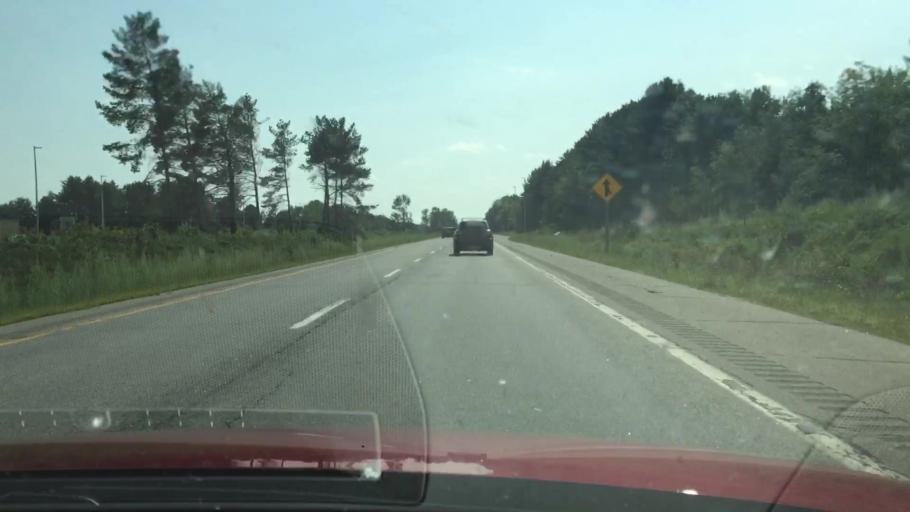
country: US
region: Maine
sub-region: Somerset County
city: Fairfield
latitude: 44.5931
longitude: -69.6171
